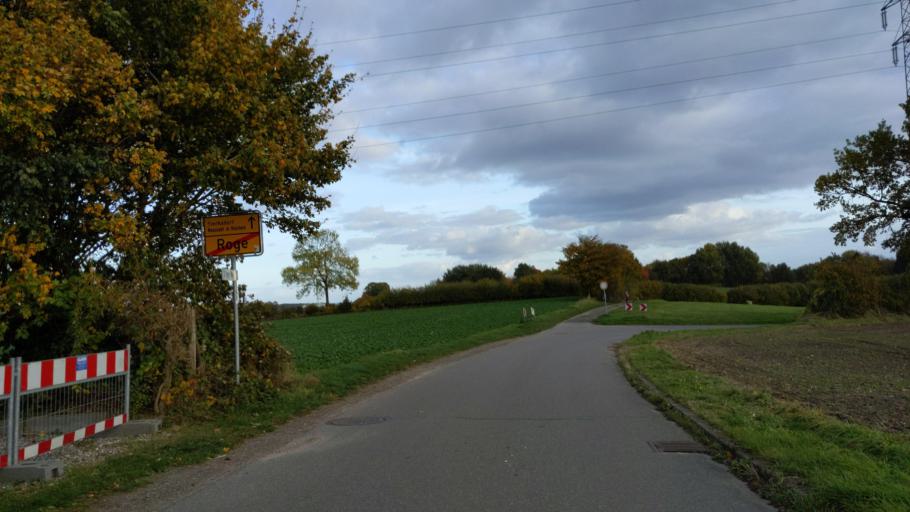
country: DE
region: Schleswig-Holstein
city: Sierksdorf
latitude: 54.0993
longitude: 10.7725
